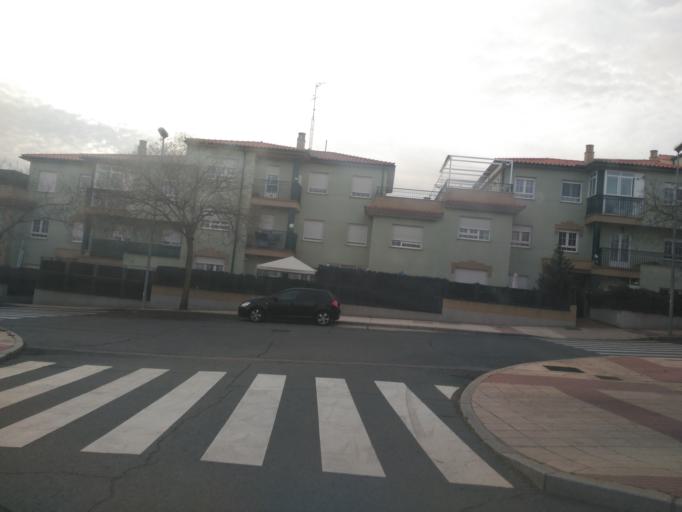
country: ES
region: Castille and Leon
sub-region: Provincia de Salamanca
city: Salamanca
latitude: 40.9629
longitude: -5.6906
